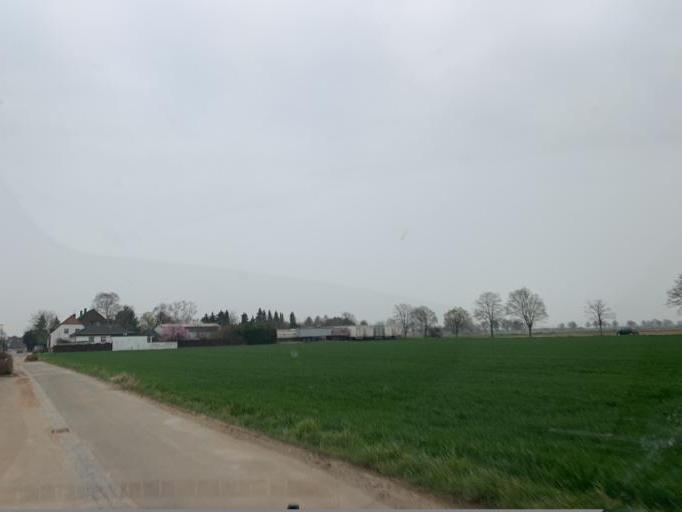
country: DE
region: North Rhine-Westphalia
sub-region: Regierungsbezirk Koln
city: Elsdorf
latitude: 50.8818
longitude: 6.5960
